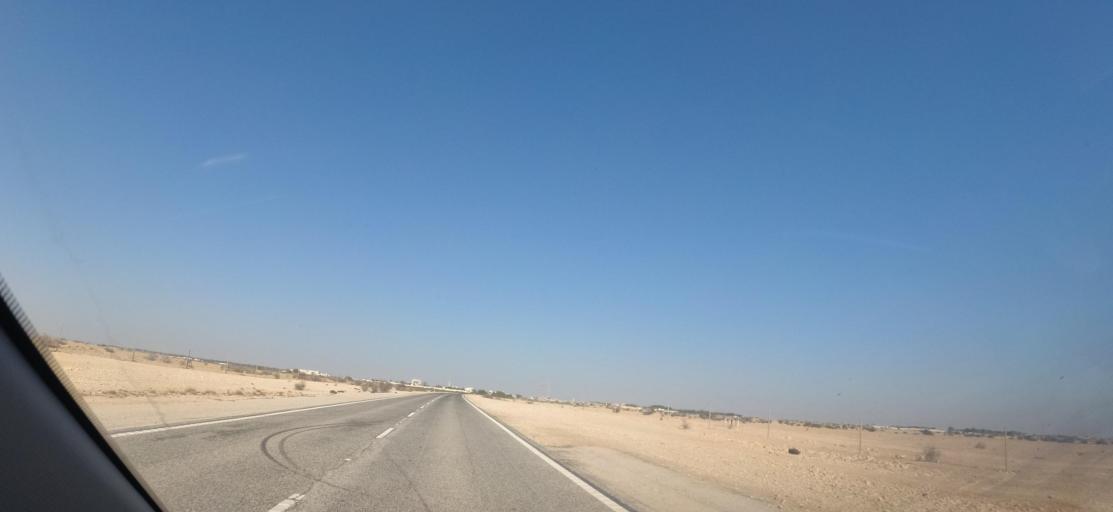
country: QA
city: Al Ghuwayriyah
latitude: 25.8188
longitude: 51.2354
